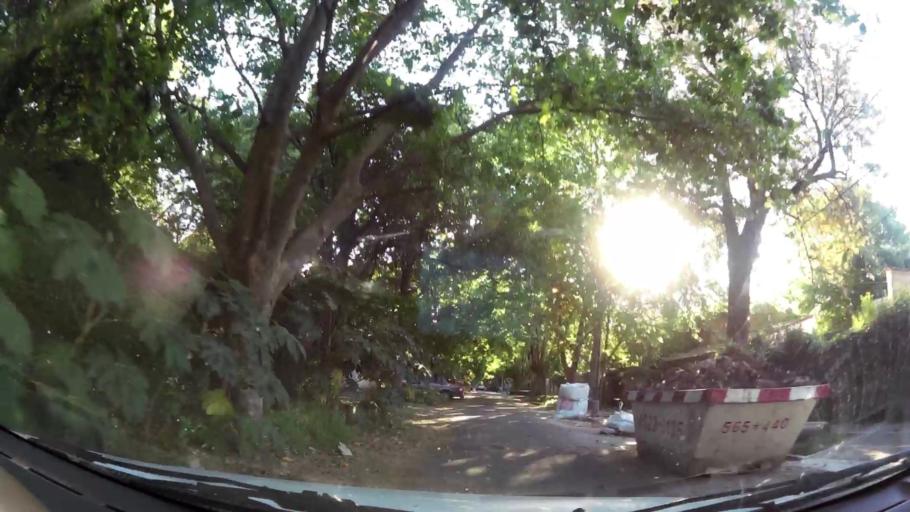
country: AR
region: Buenos Aires
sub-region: Partido de San Isidro
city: San Isidro
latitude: -34.4762
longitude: -58.5477
